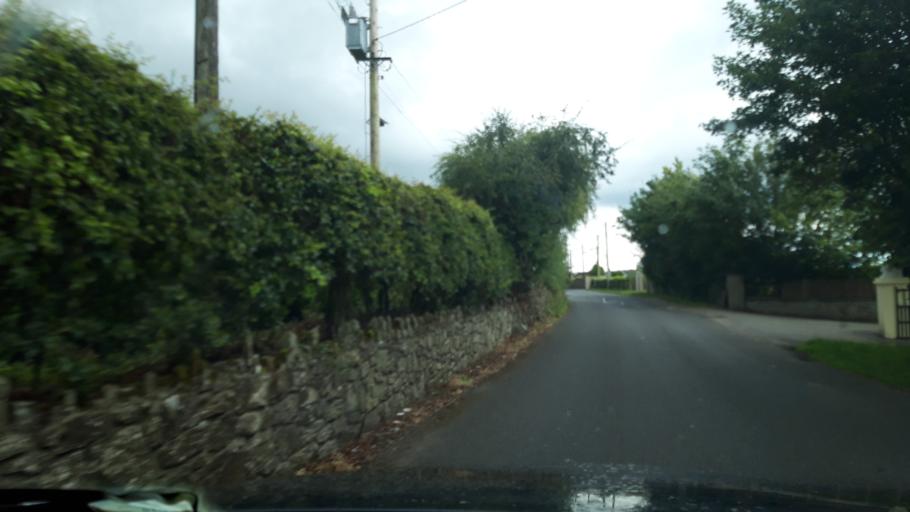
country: IE
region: Leinster
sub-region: Wicklow
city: Baltinglass
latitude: 52.9457
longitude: -6.7067
